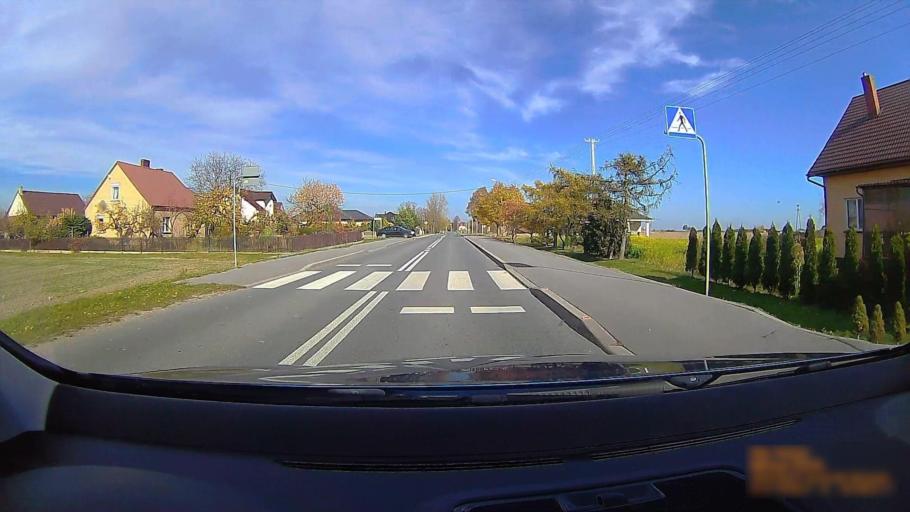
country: PL
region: Greater Poland Voivodeship
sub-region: Powiat kepinski
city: Kepno
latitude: 51.3276
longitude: 18.0160
